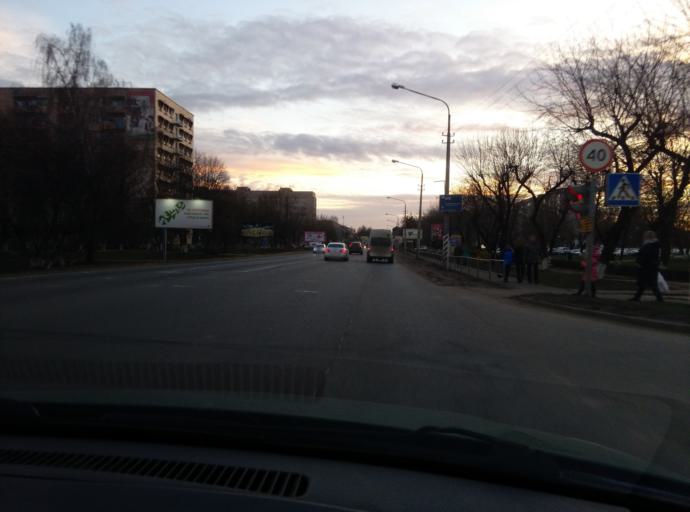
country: BY
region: Minsk
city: Horad Barysaw
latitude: 54.2195
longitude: 28.4913
